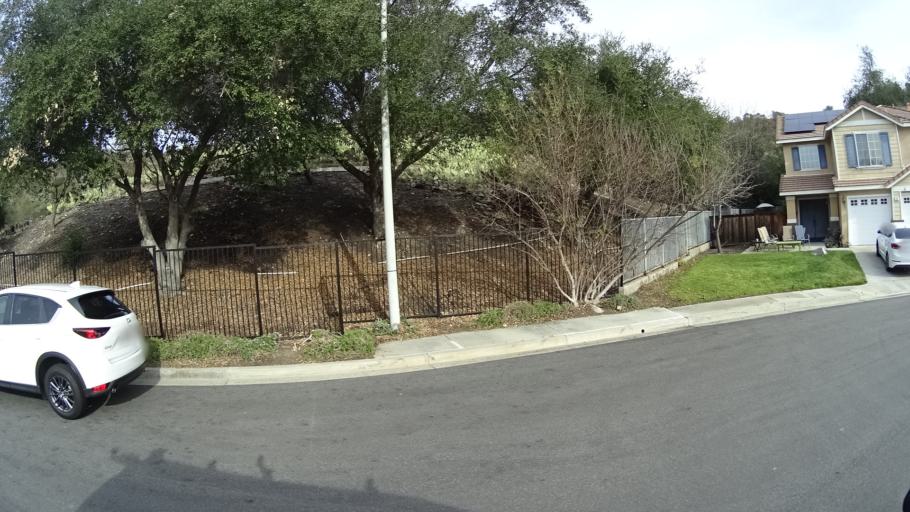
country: US
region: California
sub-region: Orange County
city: Coto De Caza
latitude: 33.5952
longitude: -117.5983
